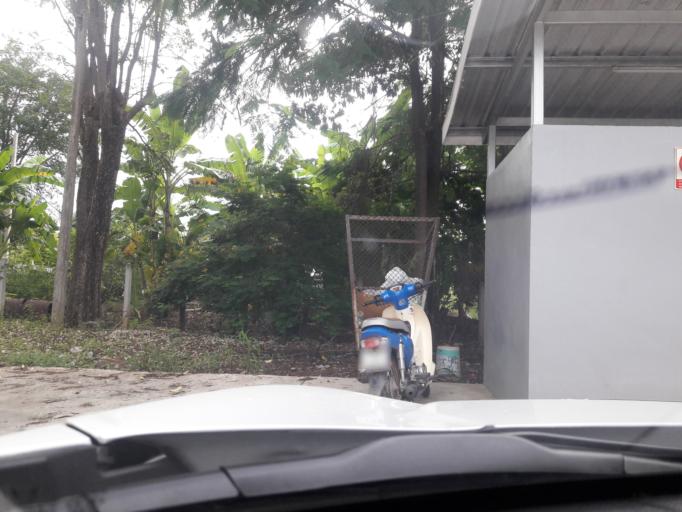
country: TH
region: Lop Buri
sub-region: Amphoe Tha Luang
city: Tha Luang
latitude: 15.0690
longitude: 101.1127
